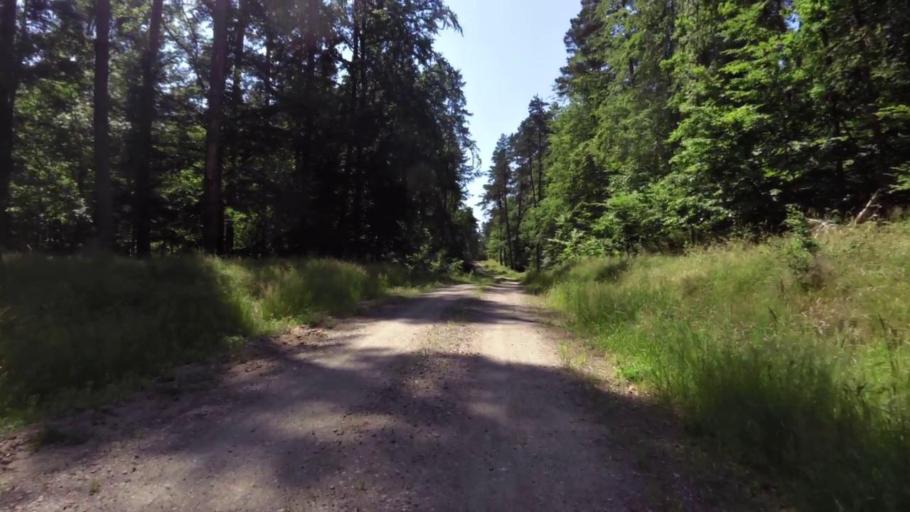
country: PL
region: West Pomeranian Voivodeship
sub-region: Powiat swidwinski
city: Polczyn-Zdroj
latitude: 53.8075
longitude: 16.1230
